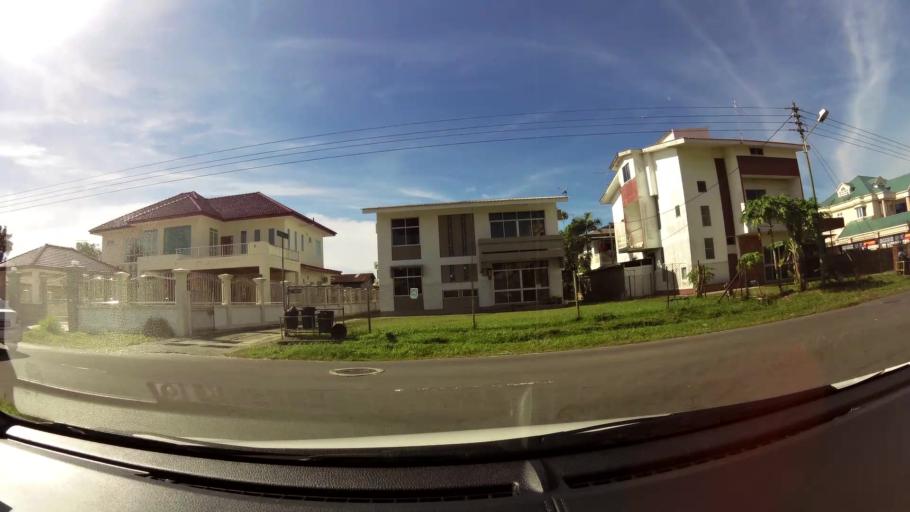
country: BN
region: Belait
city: Kuala Belait
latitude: 4.5855
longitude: 114.2137
